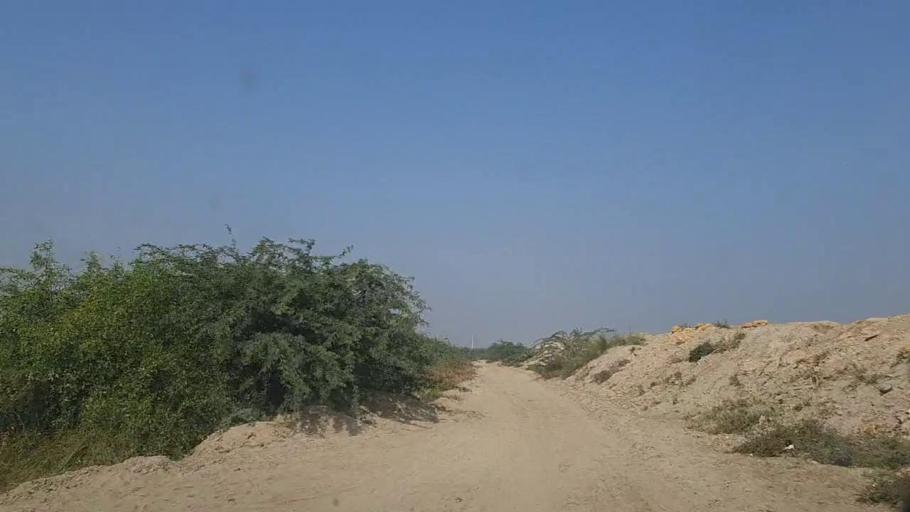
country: PK
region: Sindh
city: Thatta
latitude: 24.6602
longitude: 67.9264
